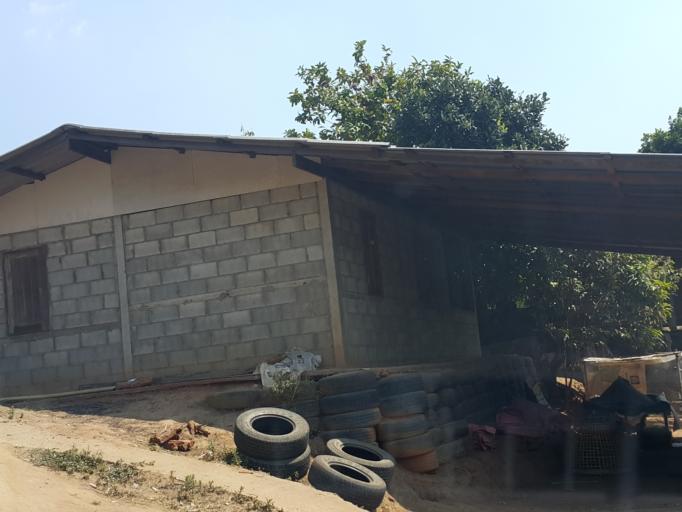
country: TH
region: Chiang Mai
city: Samoeng
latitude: 18.8877
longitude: 98.7736
